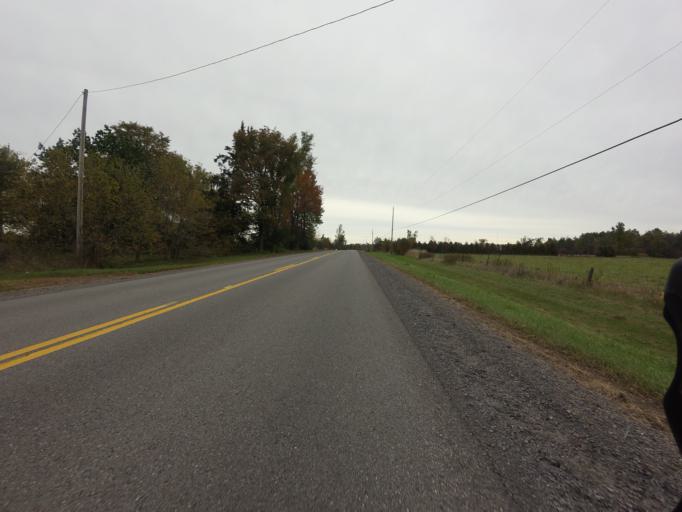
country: CA
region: Ontario
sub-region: Lanark County
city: Smiths Falls
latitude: 44.8597
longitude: -75.8097
